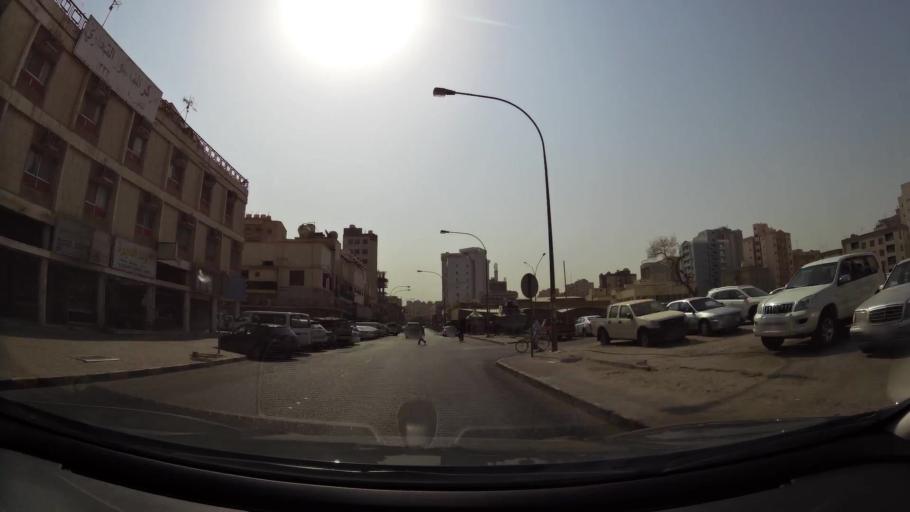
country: KW
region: Muhafazat Hawalli
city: Hawalli
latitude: 29.3423
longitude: 48.0135
